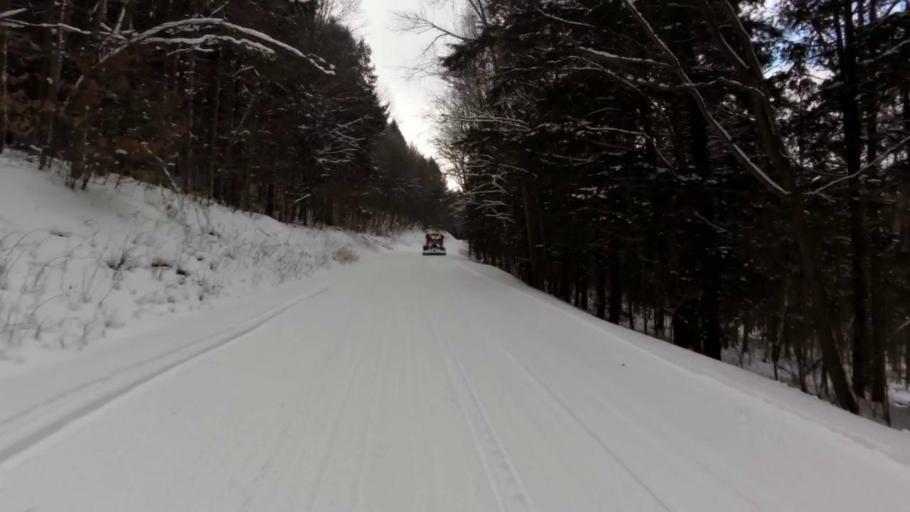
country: US
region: New York
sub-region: Cattaraugus County
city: Salamanca
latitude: 42.0650
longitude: -78.7632
